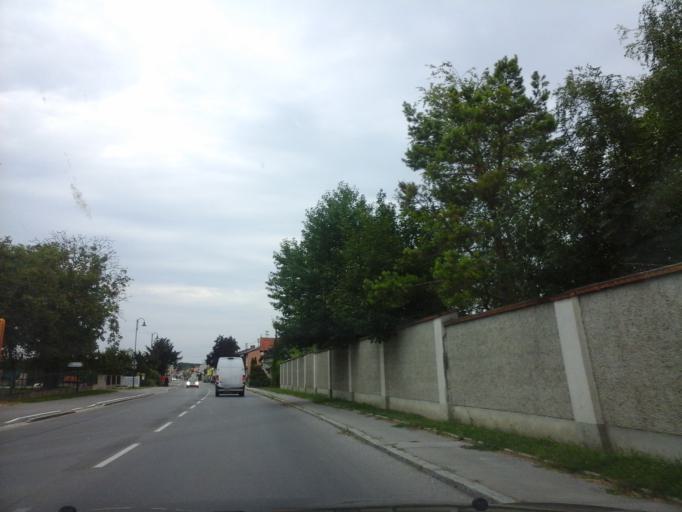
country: AT
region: Lower Austria
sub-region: Politischer Bezirk Ganserndorf
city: Orth an der Donau
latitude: 48.1476
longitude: 16.6990
